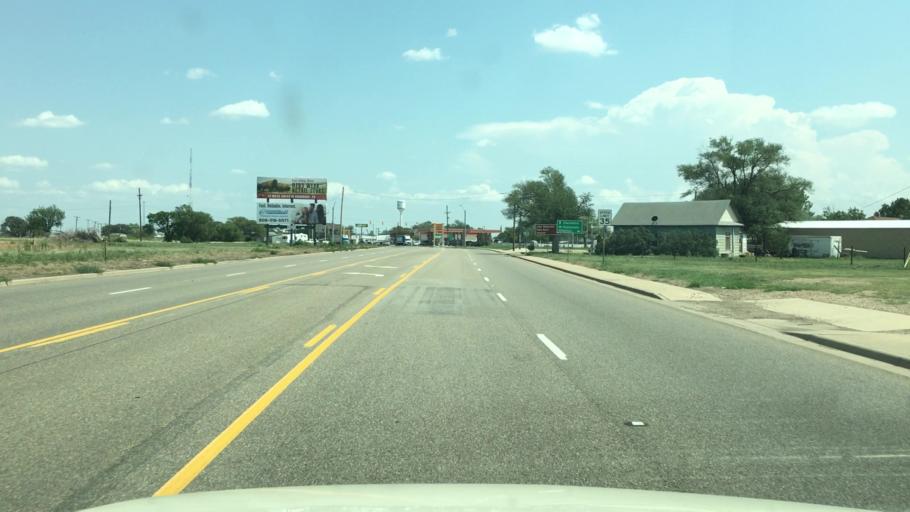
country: US
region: Texas
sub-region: Armstrong County
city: Claude
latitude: 35.1132
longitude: -101.3658
